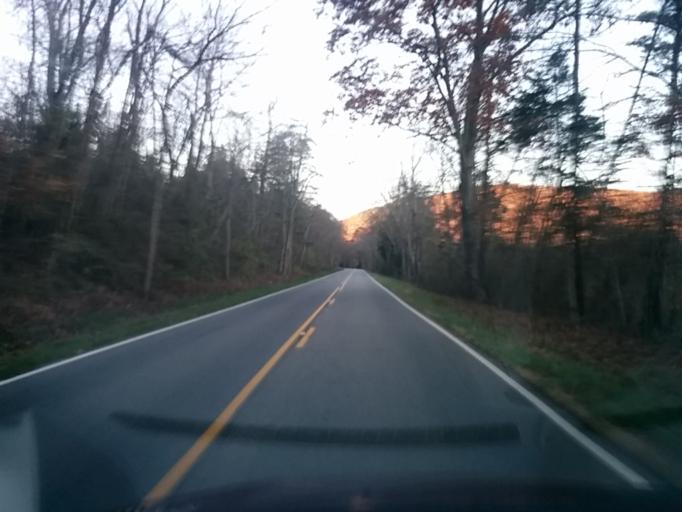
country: US
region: Virginia
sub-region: Rockbridge County
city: East Lexington
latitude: 37.9562
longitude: -79.4702
